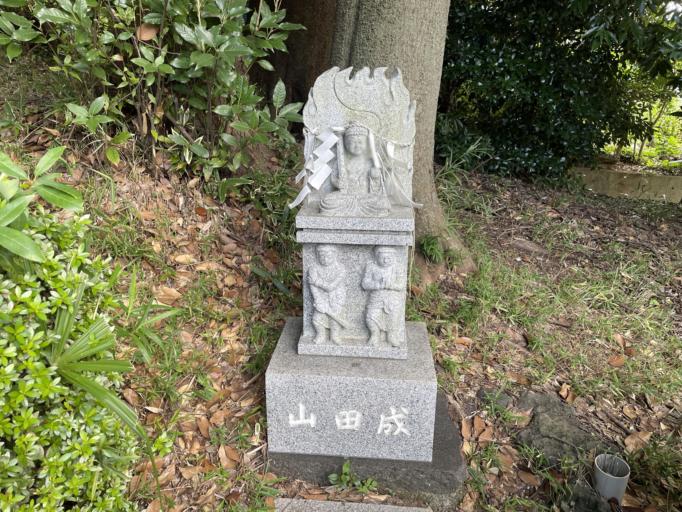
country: JP
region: Chiba
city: Matsudo
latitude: 35.8082
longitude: 139.9443
